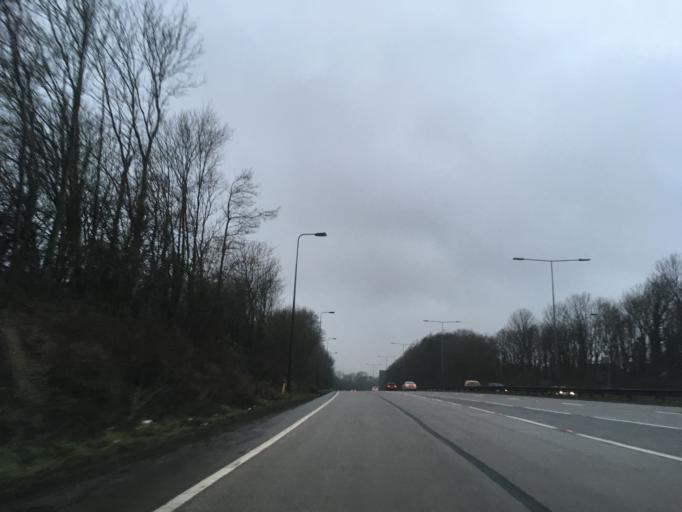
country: GB
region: Wales
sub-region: Cardiff
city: Radyr
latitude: 51.4683
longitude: -3.2741
